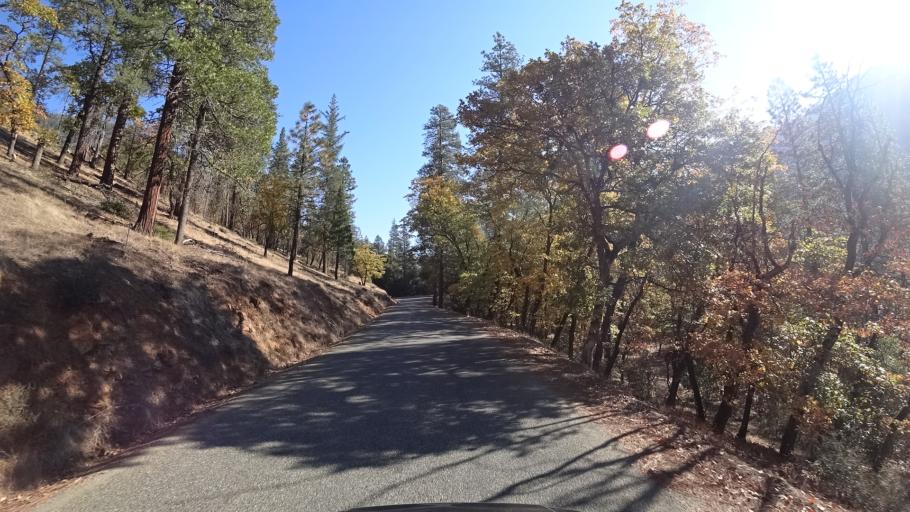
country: US
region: California
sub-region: Siskiyou County
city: Happy Camp
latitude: 41.6918
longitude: -123.0736
